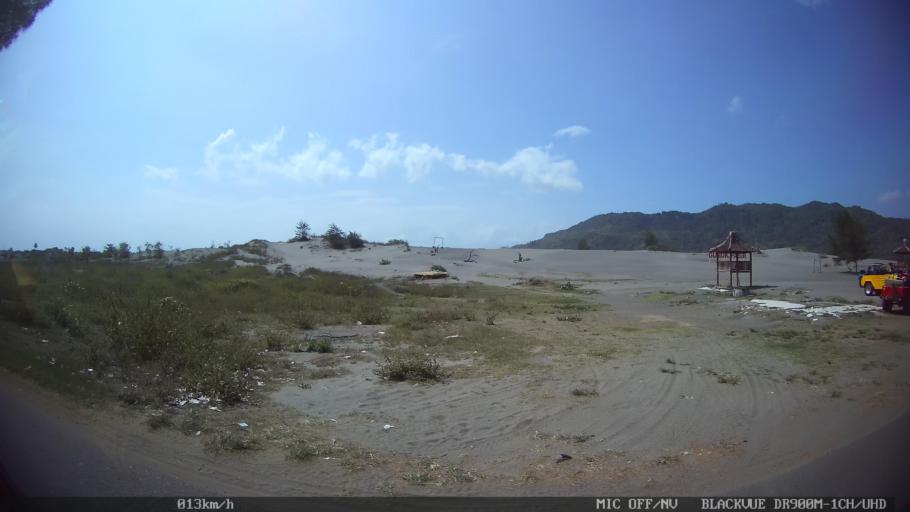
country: ID
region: Daerah Istimewa Yogyakarta
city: Pundong
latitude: -8.0182
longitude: 110.3152
